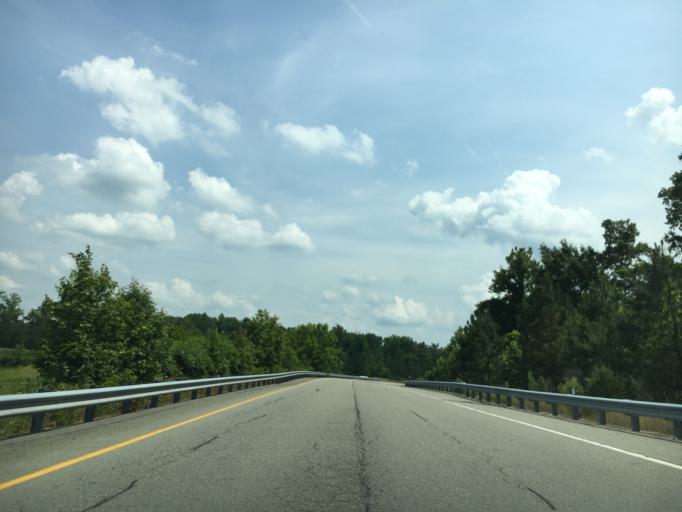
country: US
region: Virginia
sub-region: Henrico County
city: Short Pump
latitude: 37.6627
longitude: -77.6606
